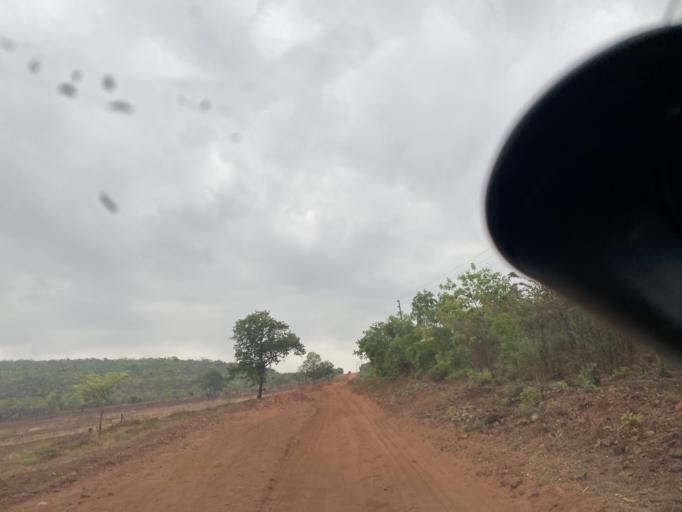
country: ZM
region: Lusaka
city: Chongwe
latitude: -15.1791
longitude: 28.7631
